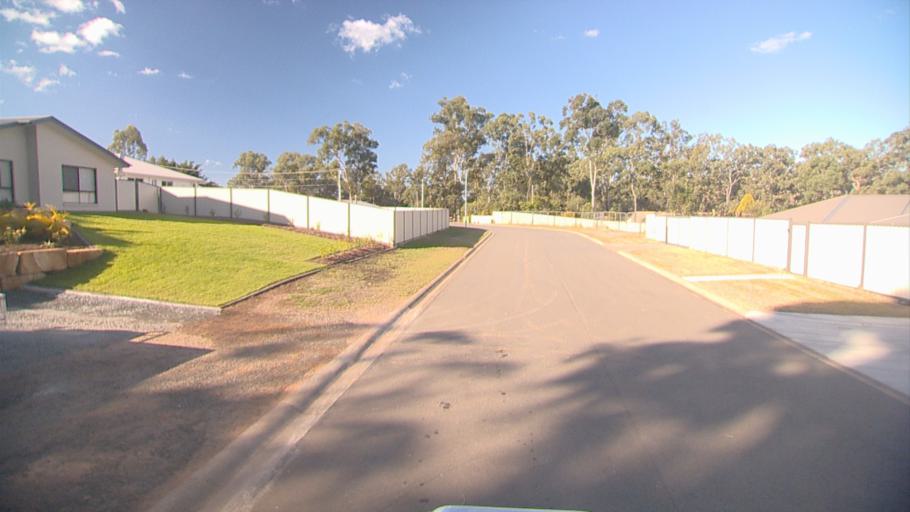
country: AU
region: Queensland
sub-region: Logan
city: Beenleigh
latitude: -27.6724
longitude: 153.1966
